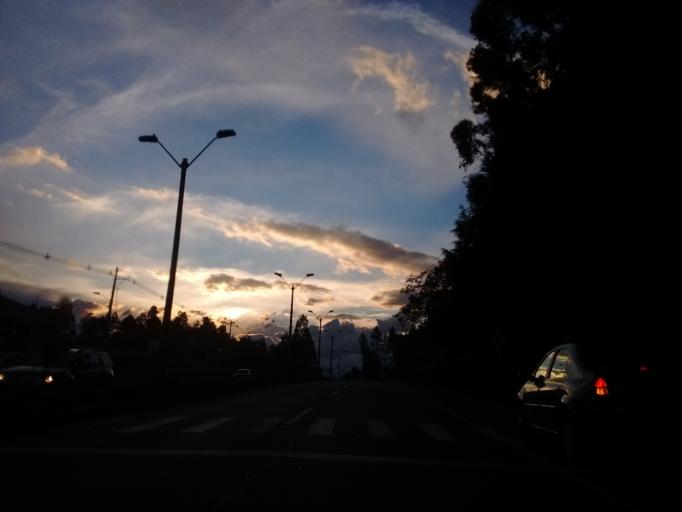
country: CO
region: Antioquia
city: Envigado
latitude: 6.1534
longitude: -75.5408
